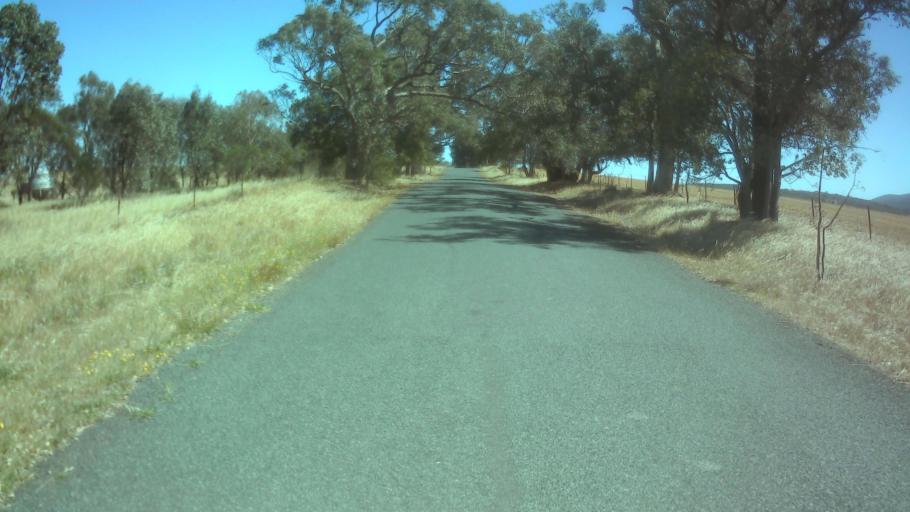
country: AU
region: New South Wales
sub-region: Weddin
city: Grenfell
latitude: -33.9444
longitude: 148.3882
